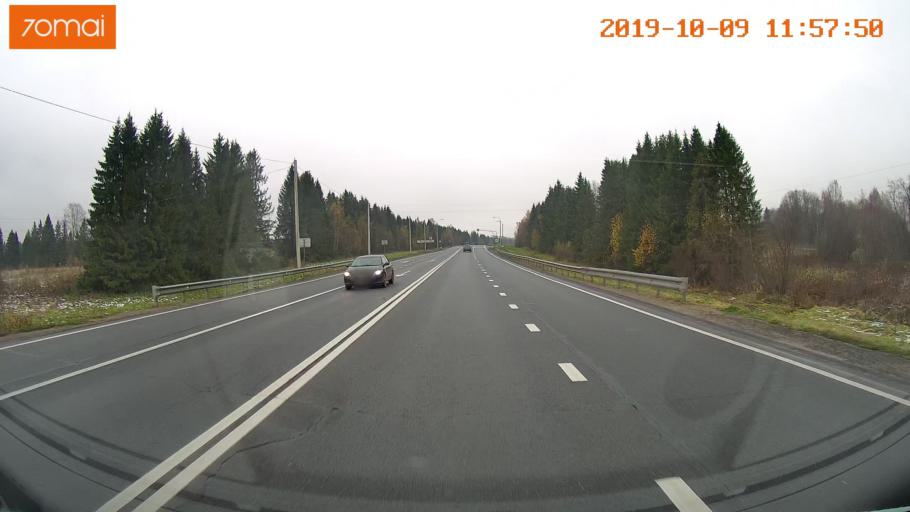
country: RU
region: Vologda
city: Gryazovets
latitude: 58.7266
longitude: 40.2949
